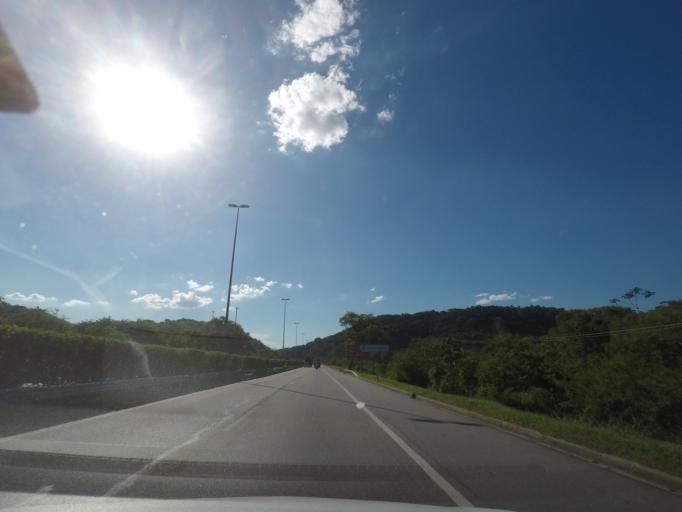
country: BR
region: Rio de Janeiro
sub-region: Petropolis
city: Petropolis
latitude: -22.6558
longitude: -43.1383
